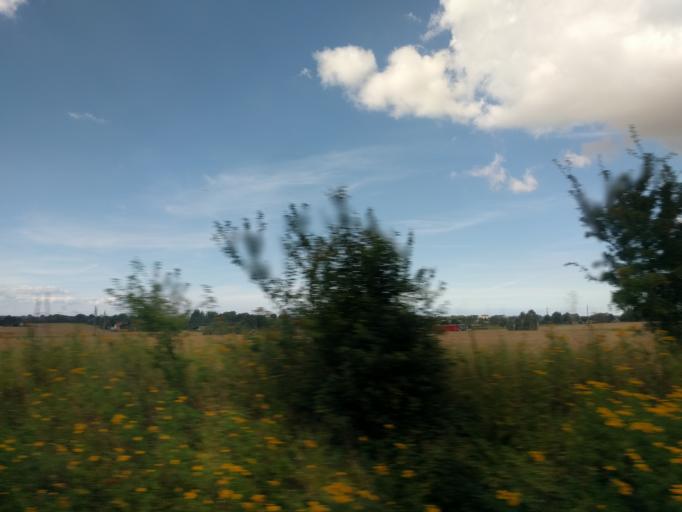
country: DK
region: Zealand
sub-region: Slagelse Kommune
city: Forlev
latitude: 55.3982
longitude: 11.3036
